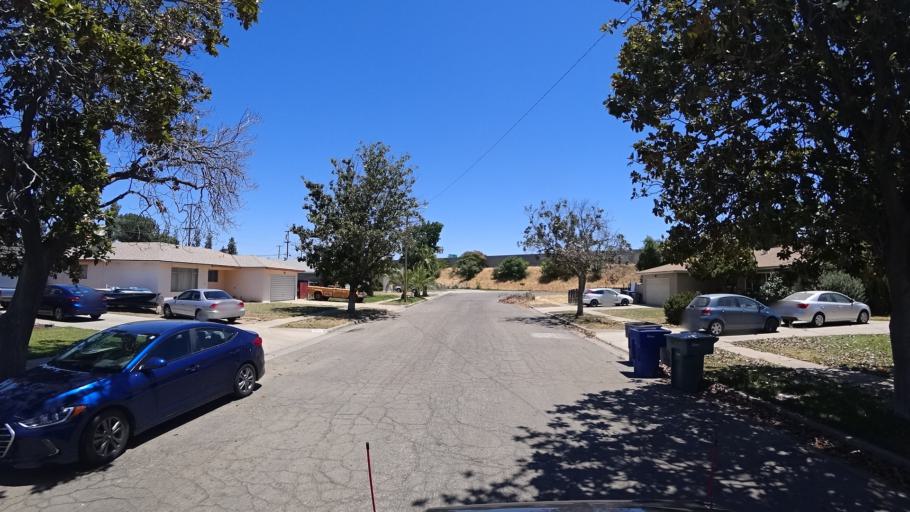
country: US
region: California
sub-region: Fresno County
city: Tarpey Village
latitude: 36.8006
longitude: -119.7425
